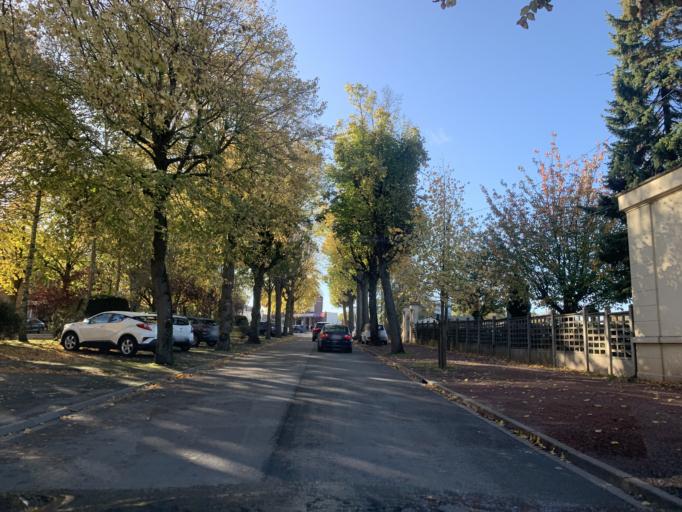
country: FR
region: Nord-Pas-de-Calais
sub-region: Departement du Nord
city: Cambrai
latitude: 50.1687
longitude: 3.2286
